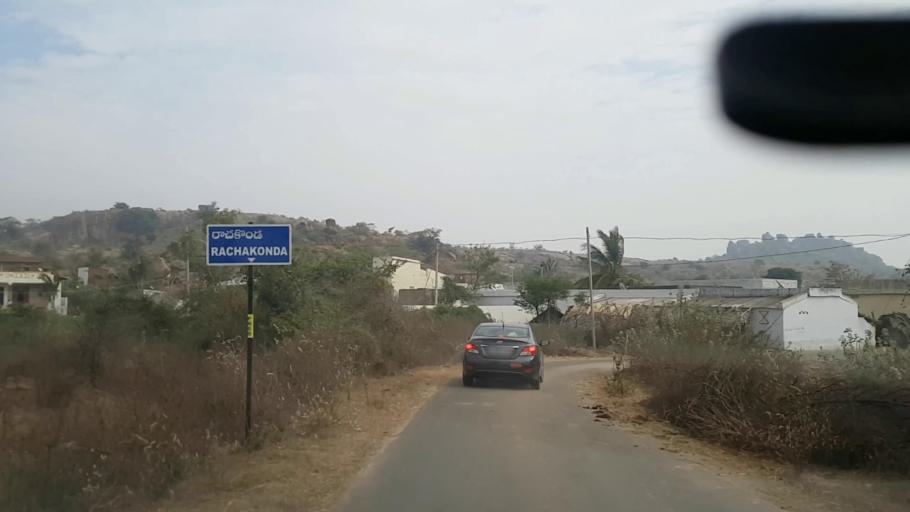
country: IN
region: Telangana
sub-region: Rangareddi
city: Lal Bahadur Nagar
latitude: 17.1797
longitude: 78.7805
